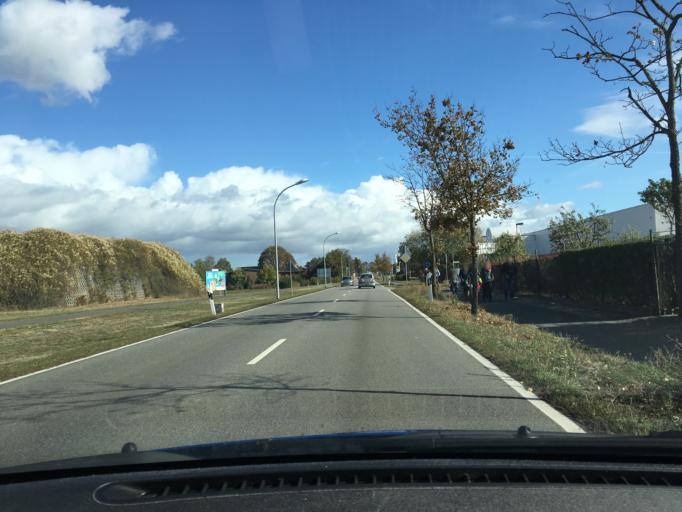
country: DE
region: Saxony-Anhalt
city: Salzwedel
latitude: 52.8421
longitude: 11.1765
